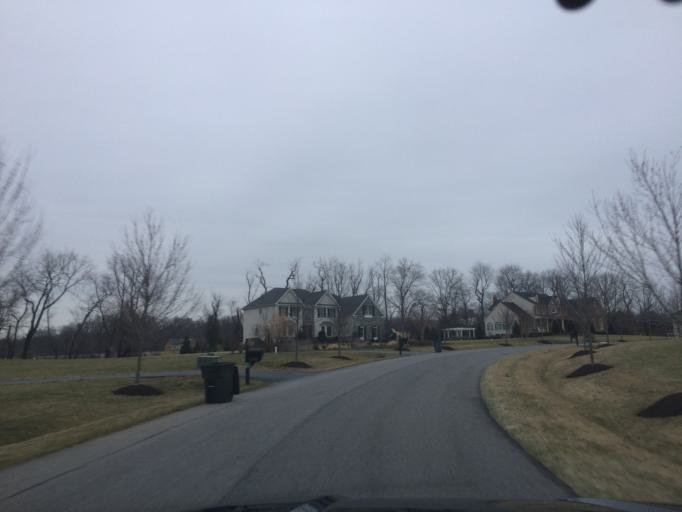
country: US
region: Maryland
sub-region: Howard County
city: Highland
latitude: 39.2679
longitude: -77.0023
